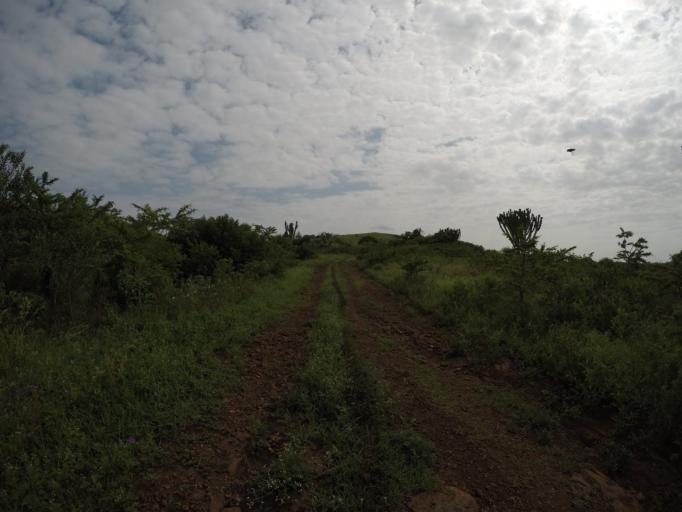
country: ZA
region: KwaZulu-Natal
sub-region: uThungulu District Municipality
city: Empangeni
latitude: -28.6244
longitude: 31.8939
